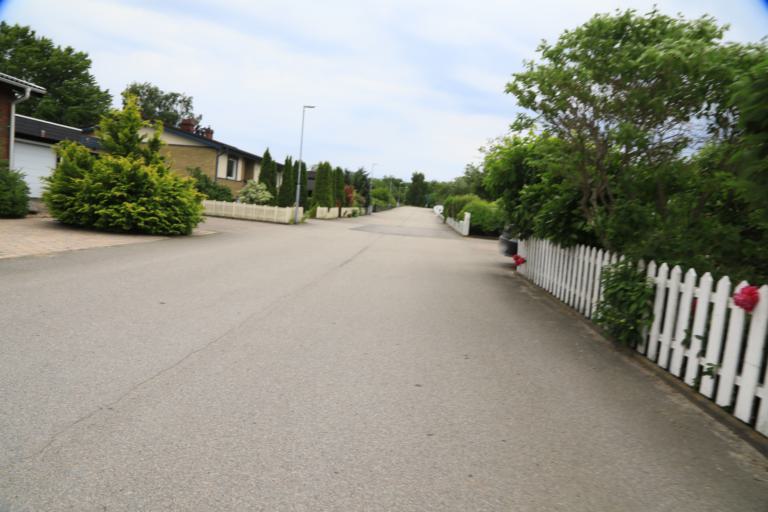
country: SE
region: Halland
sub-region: Varbergs Kommun
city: Traslovslage
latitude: 57.1019
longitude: 12.2925
